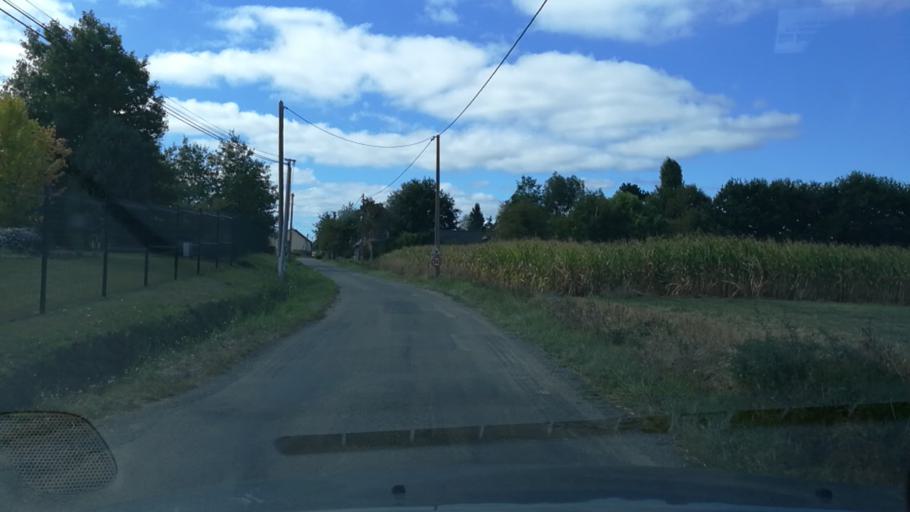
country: FR
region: Brittany
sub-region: Departement d'Ille-et-Vilaine
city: Montgermont
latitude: 48.1466
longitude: -1.7168
